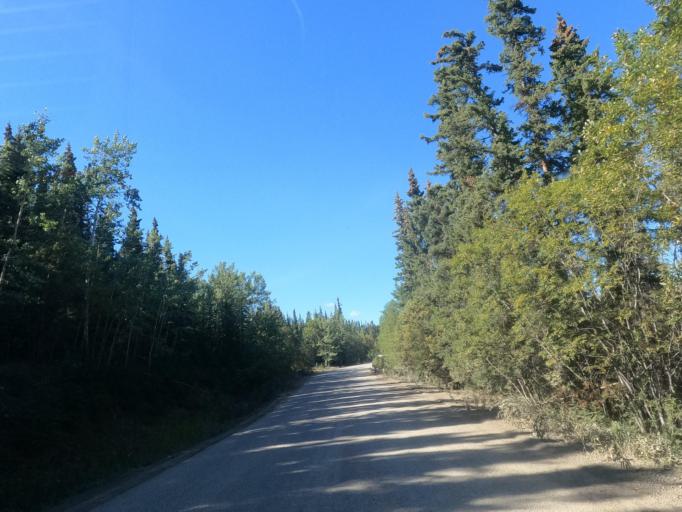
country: CA
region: Yukon
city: Whitehorse
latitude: 60.6628
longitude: -135.0312
